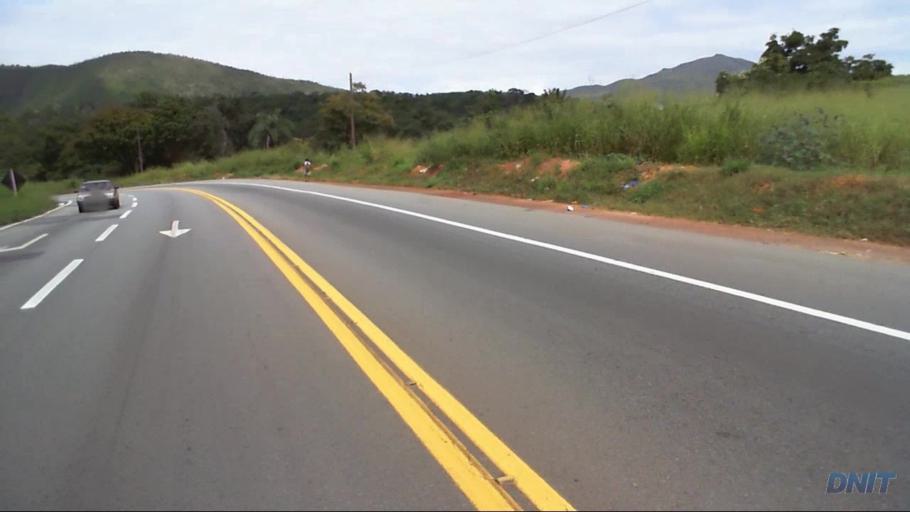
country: BR
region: Minas Gerais
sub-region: Santa Luzia
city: Santa Luzia
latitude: -19.7999
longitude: -43.7529
